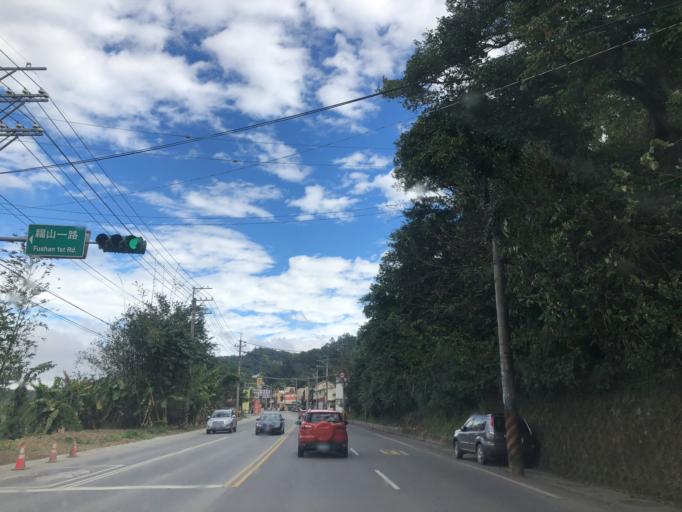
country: TW
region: Taiwan
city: Daxi
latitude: 24.8256
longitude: 121.2645
